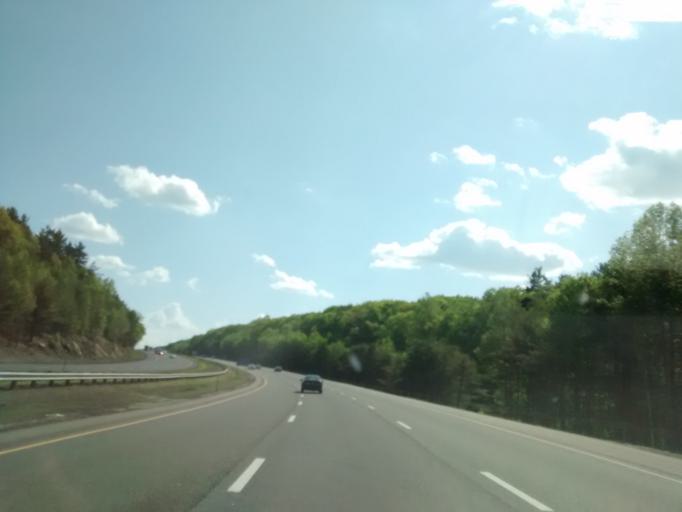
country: US
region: Massachusetts
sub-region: Hampden County
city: Holland
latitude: 42.0186
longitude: -72.1529
